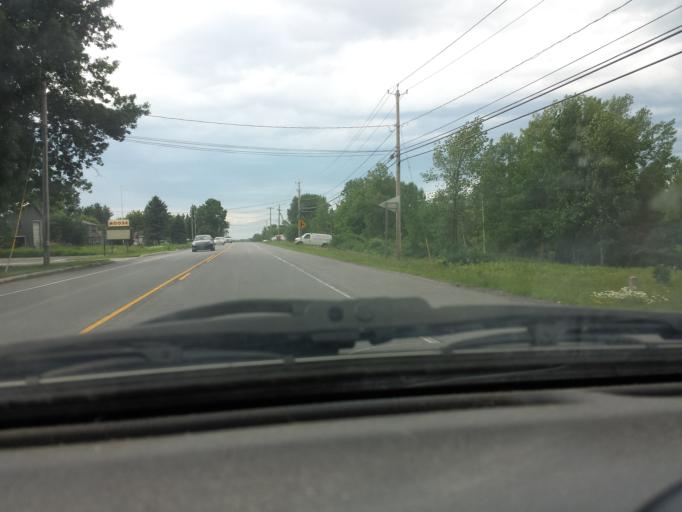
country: US
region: New York
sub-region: St. Lawrence County
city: Potsdam
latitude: 44.7098
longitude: -74.9872
